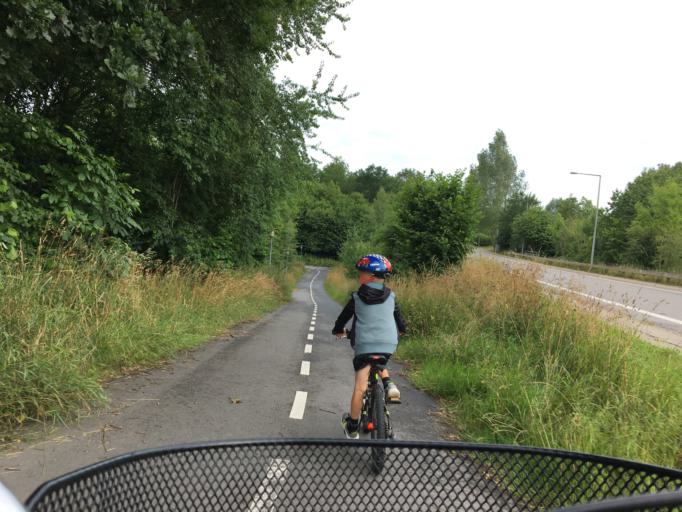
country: DK
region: South Denmark
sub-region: Fredericia Kommune
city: Snoghoj
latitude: 55.5282
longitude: 9.7319
